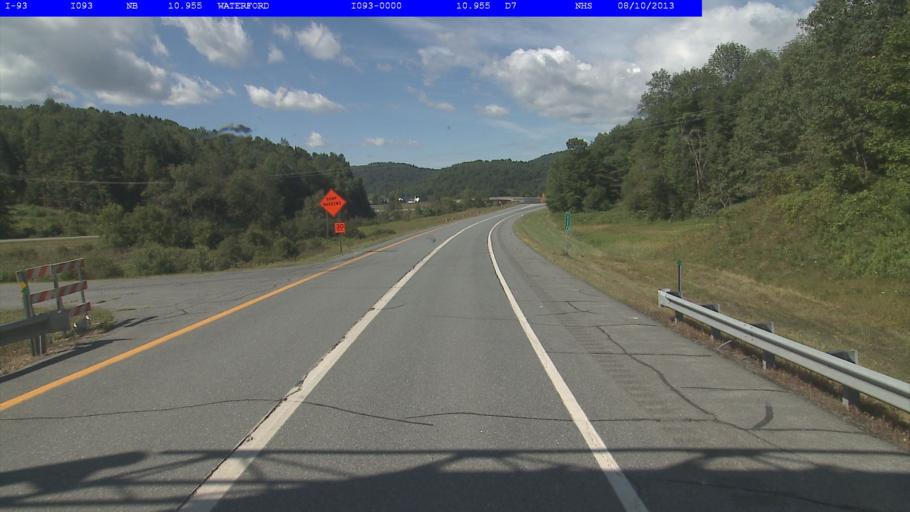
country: US
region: Vermont
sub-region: Caledonia County
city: Saint Johnsbury
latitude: 44.3990
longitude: -72.0124
